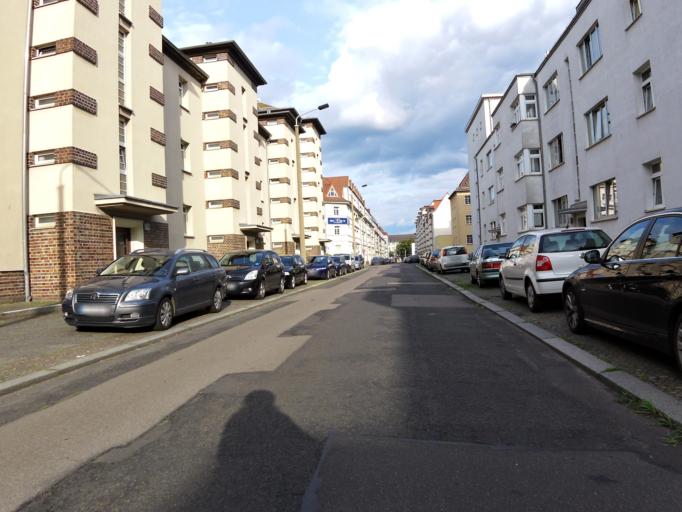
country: DE
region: Saxony
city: Leipzig
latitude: 51.3738
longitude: 12.4066
